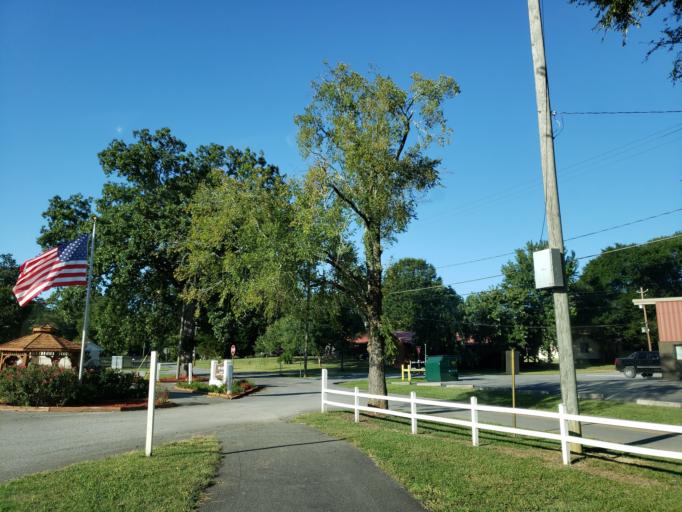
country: US
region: Georgia
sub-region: Bartow County
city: Rydal
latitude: 34.2819
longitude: -84.7456
